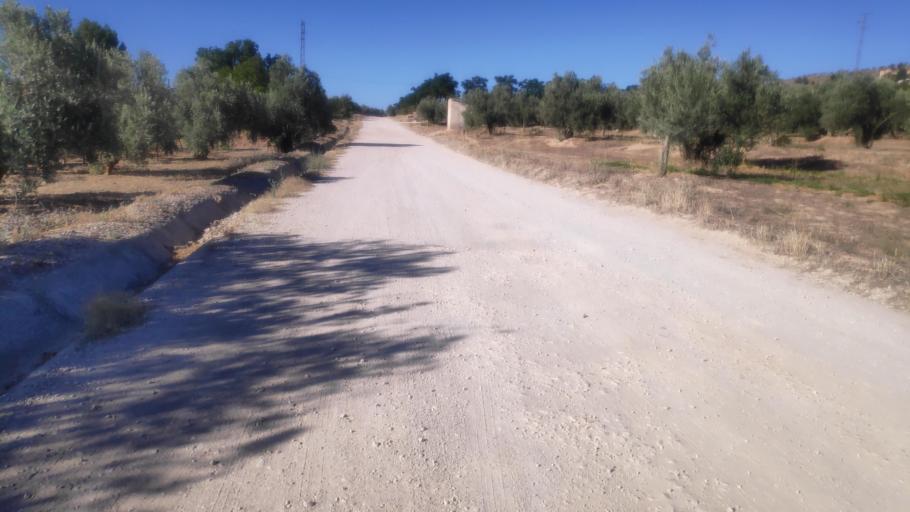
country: ES
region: Andalusia
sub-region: Provincia de Jaen
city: Pozo Alcon
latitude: 37.6683
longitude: -2.9718
